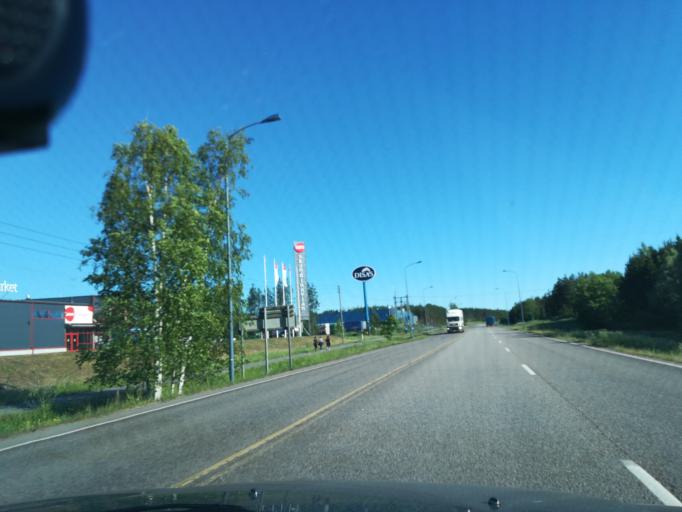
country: FI
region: South Karelia
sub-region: Imatra
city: Imatra
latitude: 61.1501
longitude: 28.8090
